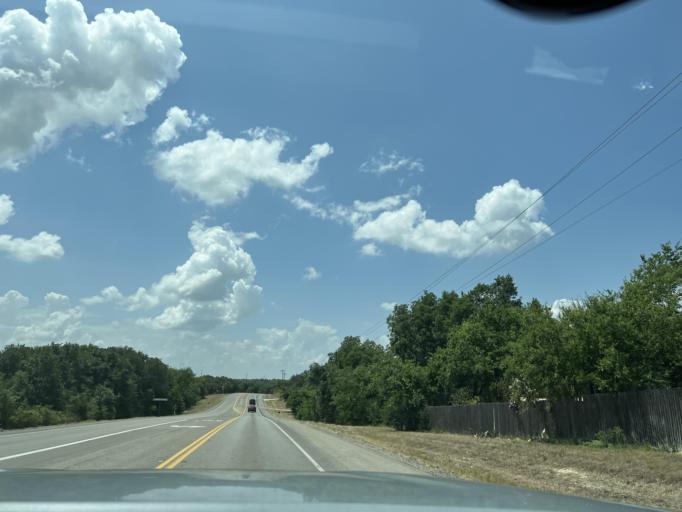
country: US
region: Texas
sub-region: Parker County
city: Weatherford
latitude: 32.8496
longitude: -97.7534
